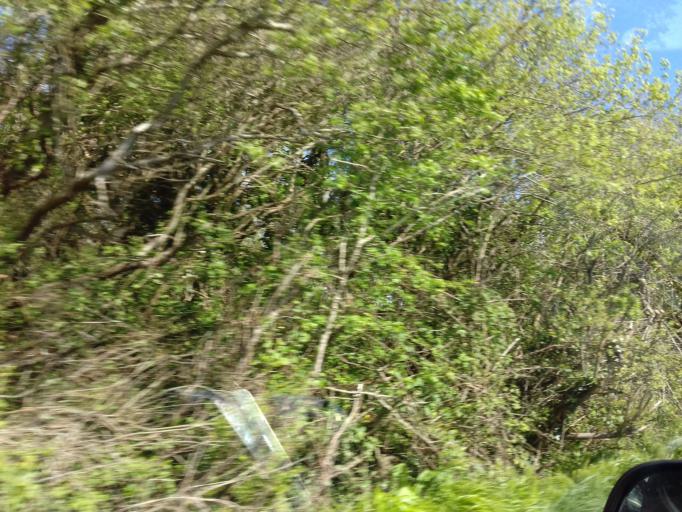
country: IE
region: Leinster
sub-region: Loch Garman
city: Castlebridge
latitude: 52.3781
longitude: -6.4276
